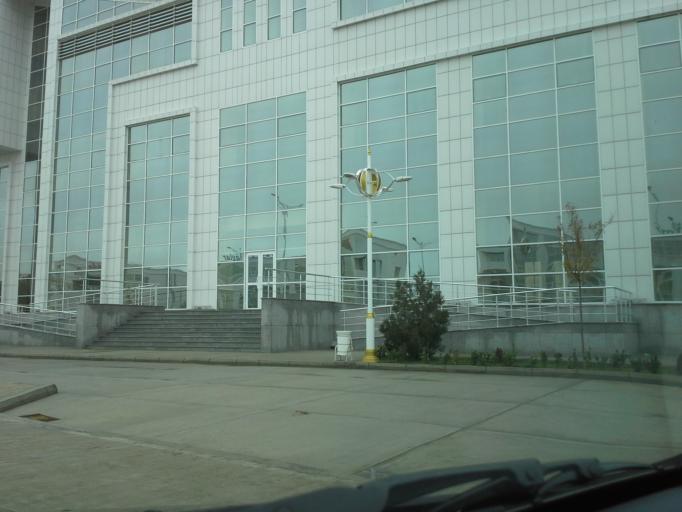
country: TM
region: Ahal
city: Ashgabat
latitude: 37.9645
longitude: 58.4121
